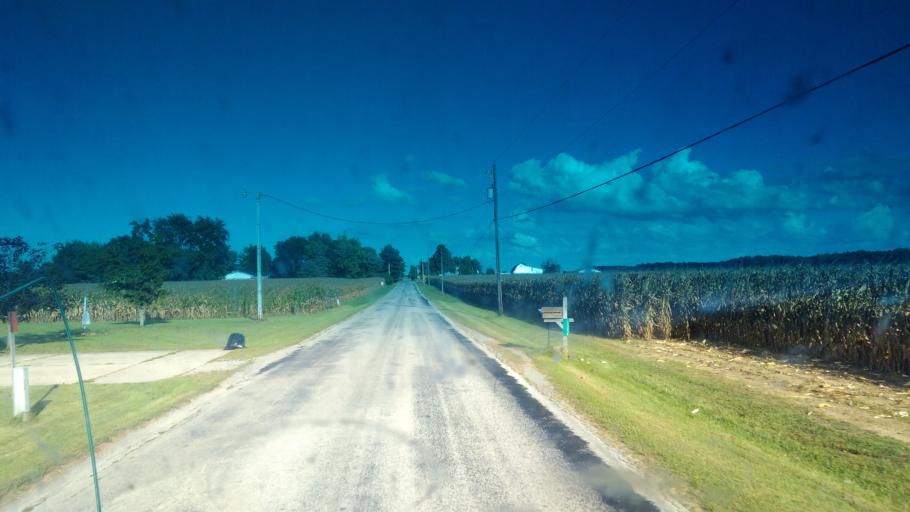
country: US
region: Ohio
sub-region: Hancock County
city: Arlington
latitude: 40.9357
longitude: -83.6462
